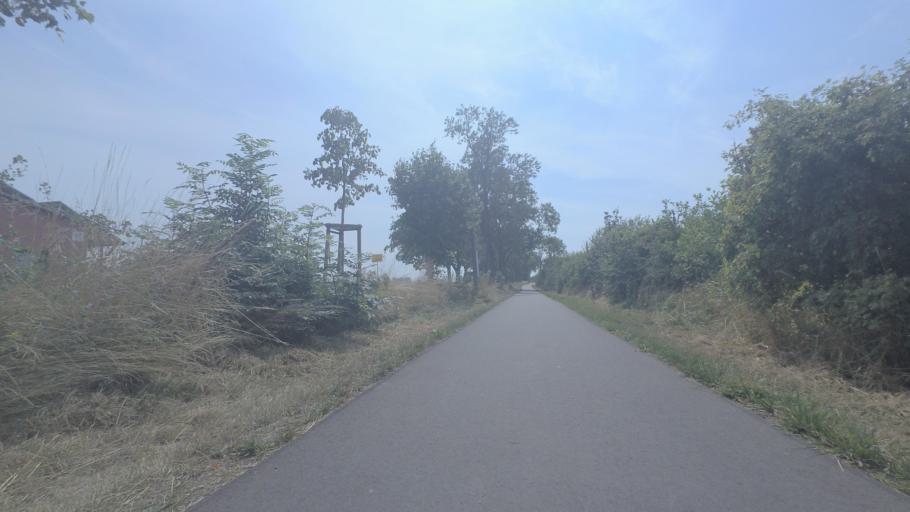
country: DE
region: Mecklenburg-Vorpommern
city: Garz
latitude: 54.2585
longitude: 13.3514
